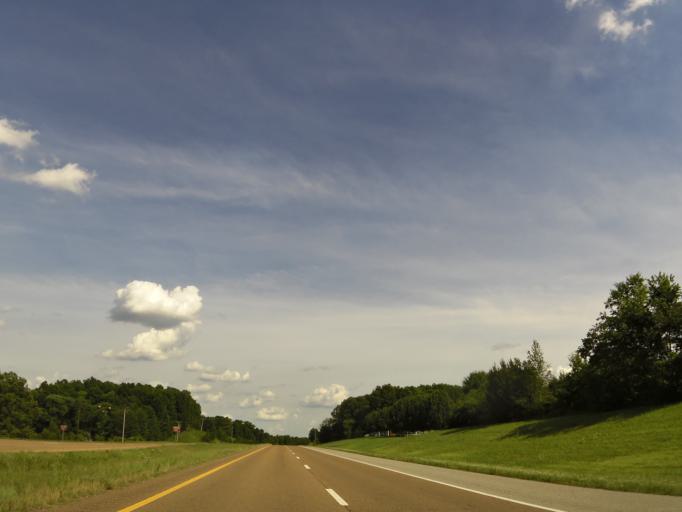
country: US
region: Tennessee
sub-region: Carroll County
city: Huntingdon
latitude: 36.0242
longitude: -88.4011
